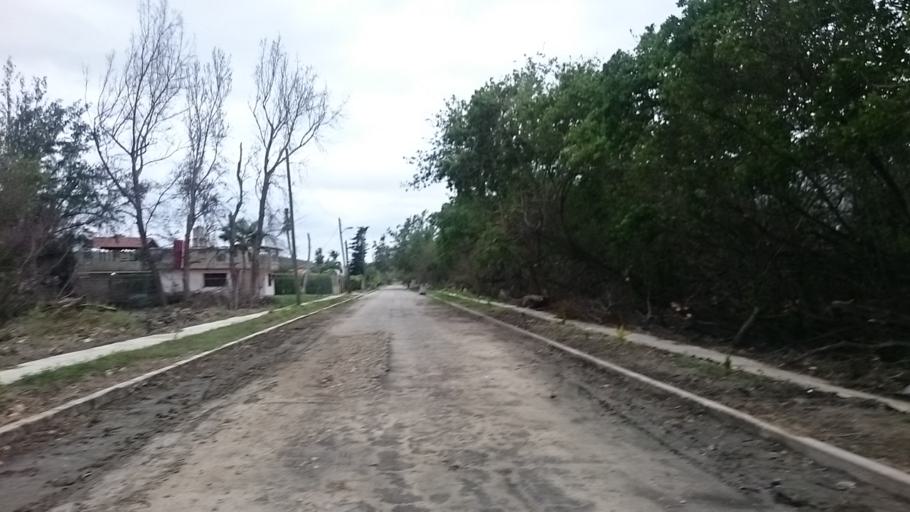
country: CU
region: Mayabeque
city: Jaruco
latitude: 23.1741
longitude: -82.1080
